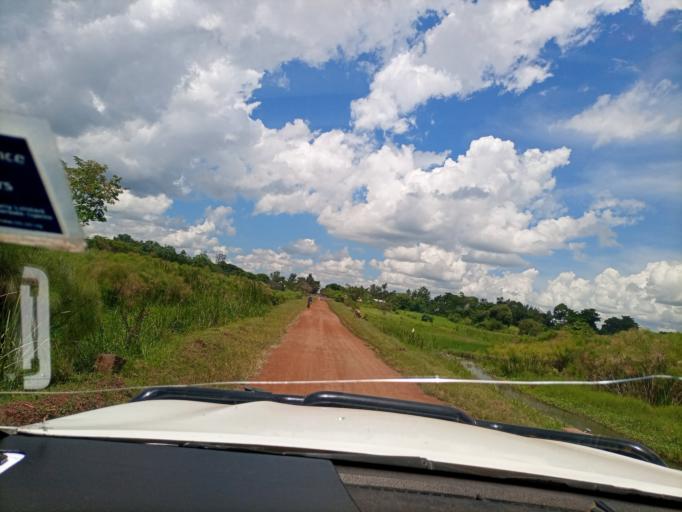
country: UG
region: Eastern Region
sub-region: Busia District
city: Busia
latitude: 0.6342
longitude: 33.9922
